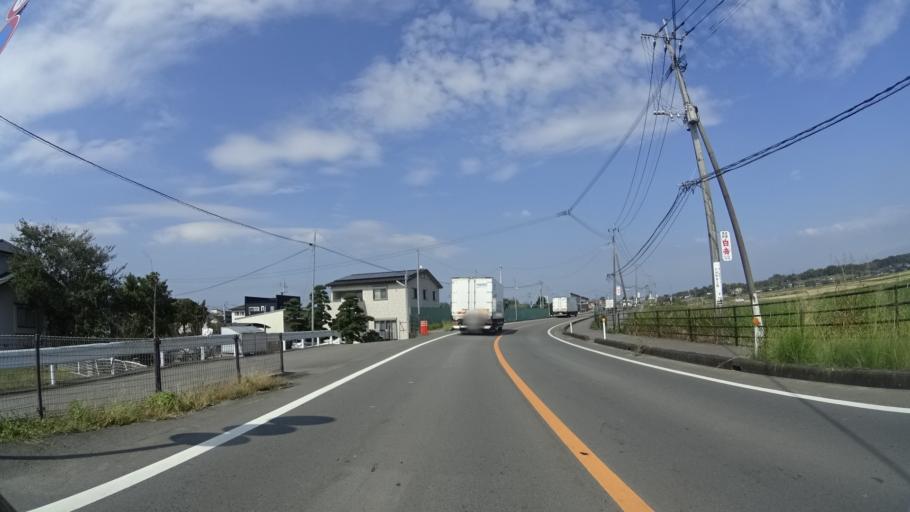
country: JP
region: Kumamoto
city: Kumamoto
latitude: 32.7384
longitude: 130.7725
